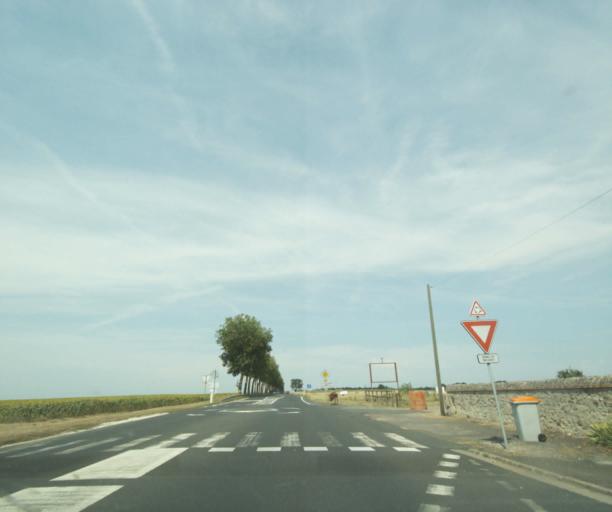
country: FR
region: Centre
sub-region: Departement d'Indre-et-Loire
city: Sainte-Maure-de-Touraine
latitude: 47.1193
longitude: 0.6217
